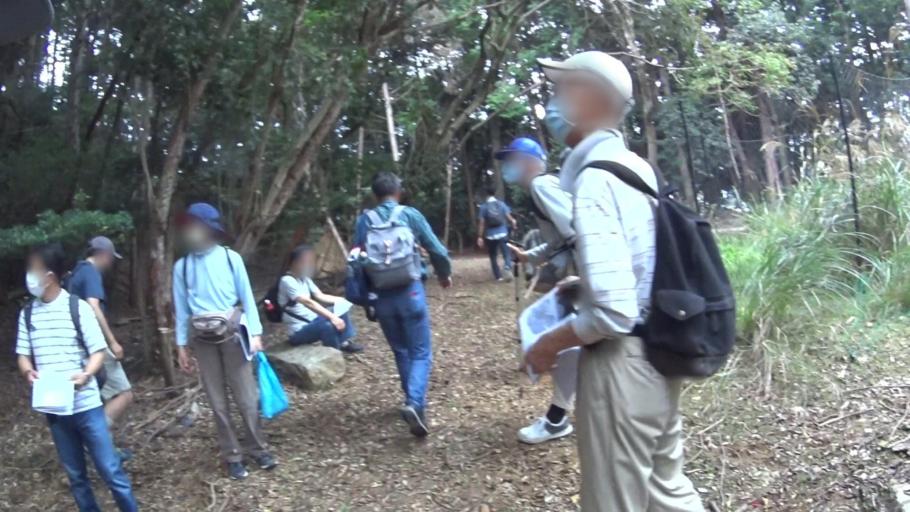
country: JP
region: Osaka
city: Kishiwada
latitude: 34.4997
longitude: 135.3325
